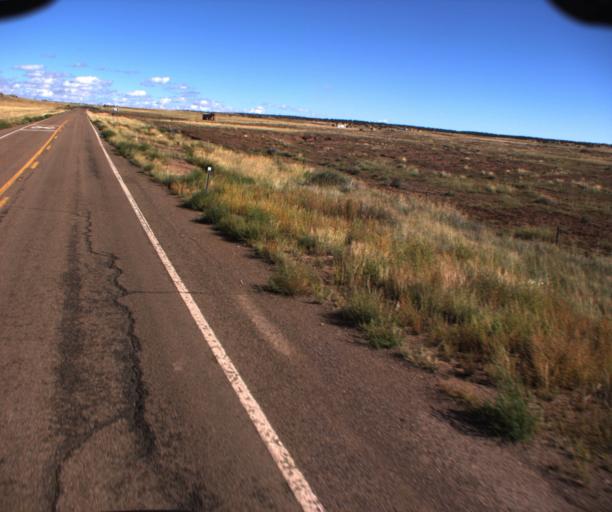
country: US
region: Arizona
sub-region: Apache County
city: Saint Johns
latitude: 34.6320
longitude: -109.3111
